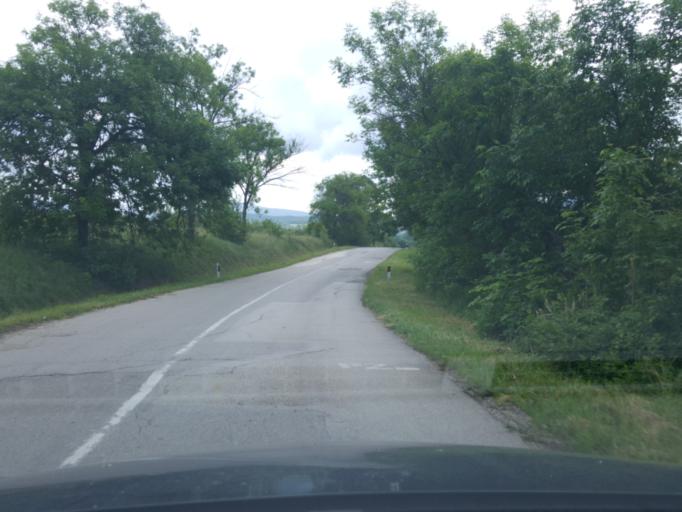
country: RS
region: Central Serbia
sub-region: Zajecarski Okrug
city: Soko Banja
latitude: 43.6456
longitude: 21.9004
